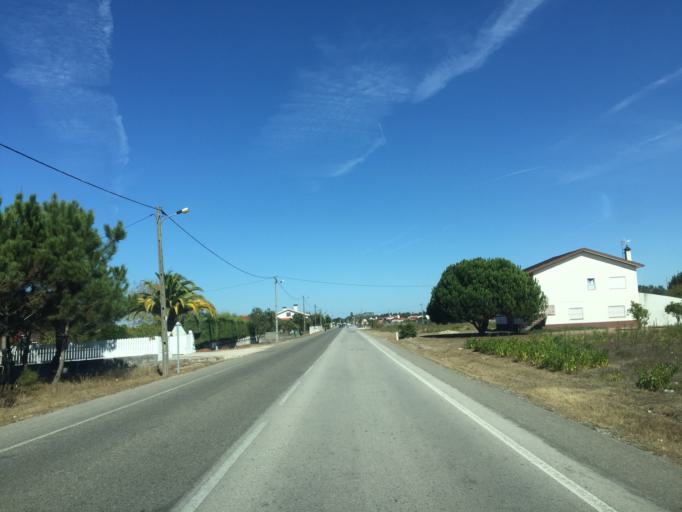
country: PT
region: Coimbra
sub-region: Figueira da Foz
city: Alhadas
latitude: 40.2269
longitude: -8.8029
